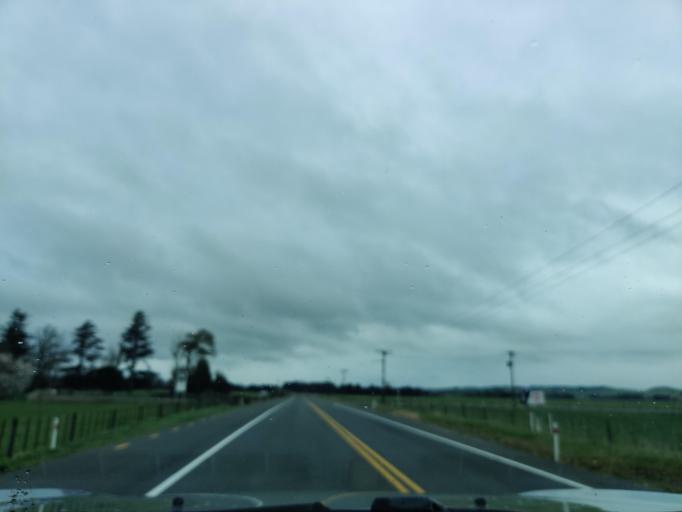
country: NZ
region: Hawke's Bay
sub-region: Hastings District
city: Hastings
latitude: -40.0021
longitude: 176.3965
